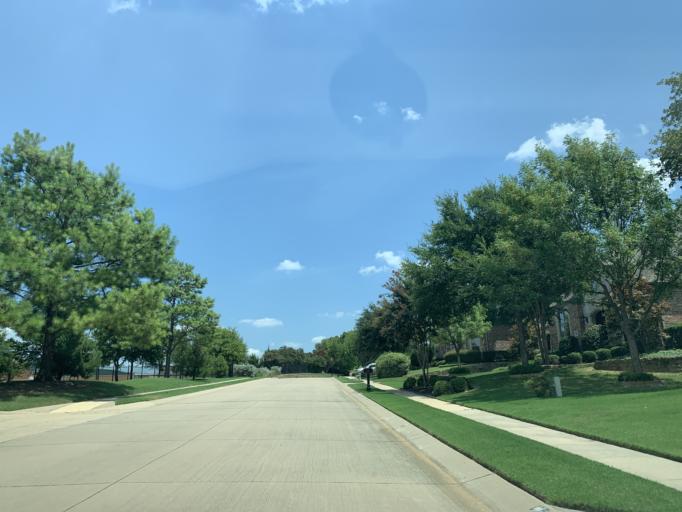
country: US
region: Texas
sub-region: Tarrant County
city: Southlake
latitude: 32.9735
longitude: -97.1543
